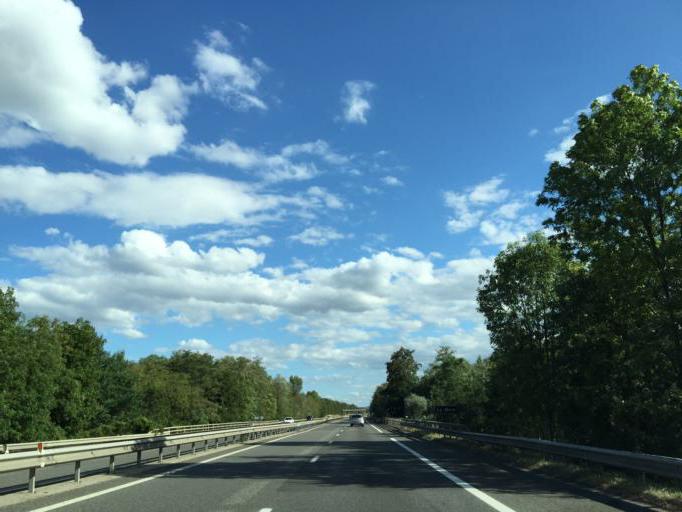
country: FR
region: Rhone-Alpes
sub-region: Departement de la Loire
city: Montrond-les-Bains
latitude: 45.6148
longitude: 4.2054
